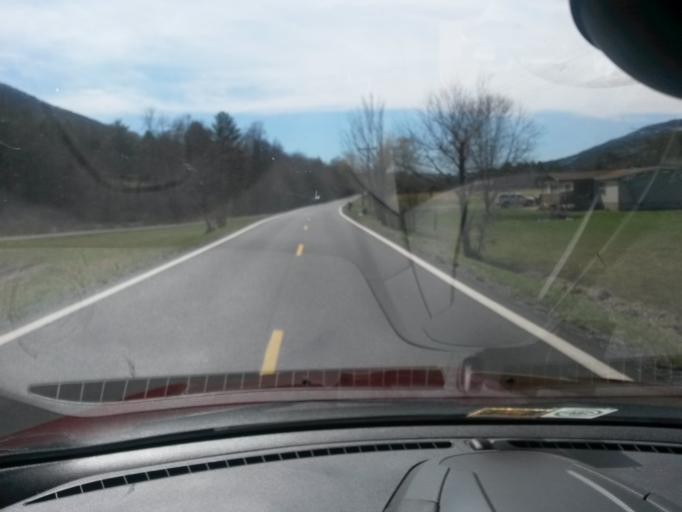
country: US
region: West Virginia
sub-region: Greenbrier County
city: White Sulphur Springs
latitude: 37.7063
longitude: -80.2109
